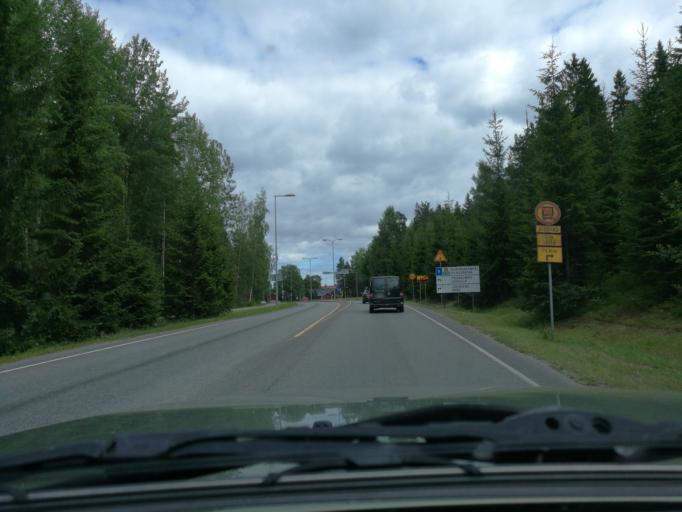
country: FI
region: Uusimaa
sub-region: Helsinki
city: Vantaa
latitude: 60.3160
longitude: 25.0691
